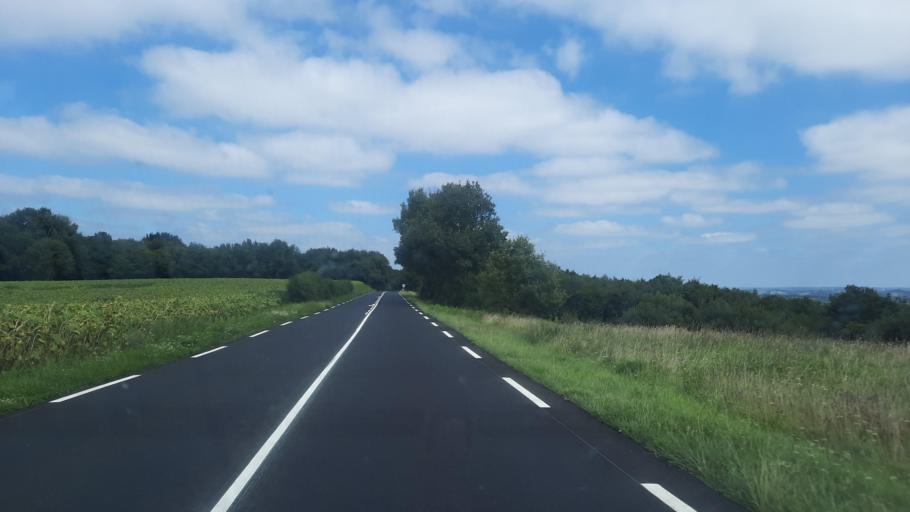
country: FR
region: Midi-Pyrenees
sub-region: Departement de la Haute-Garonne
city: Boulogne-sur-Gesse
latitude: 43.2948
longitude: 0.5835
